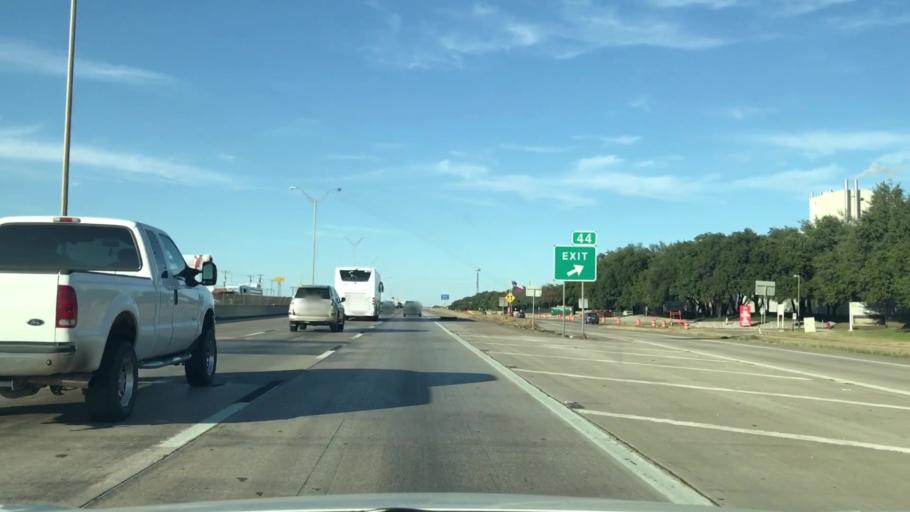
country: US
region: Texas
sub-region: Tarrant County
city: Edgecliff Village
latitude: 32.6395
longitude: -97.3215
